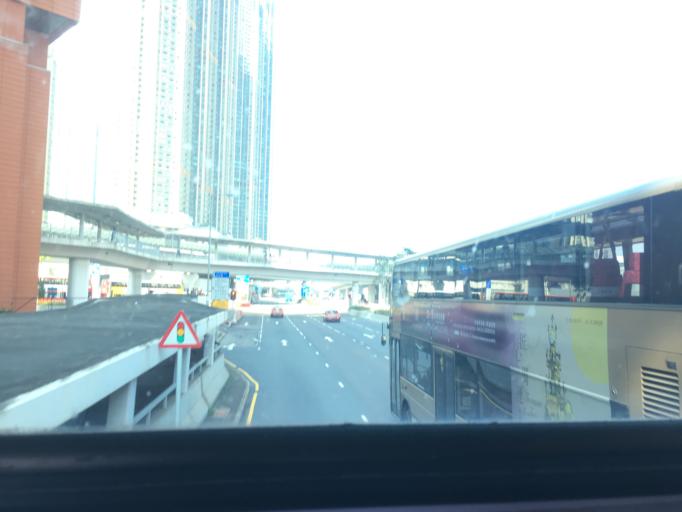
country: HK
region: Kowloon City
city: Kowloon
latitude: 22.3060
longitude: 114.1664
